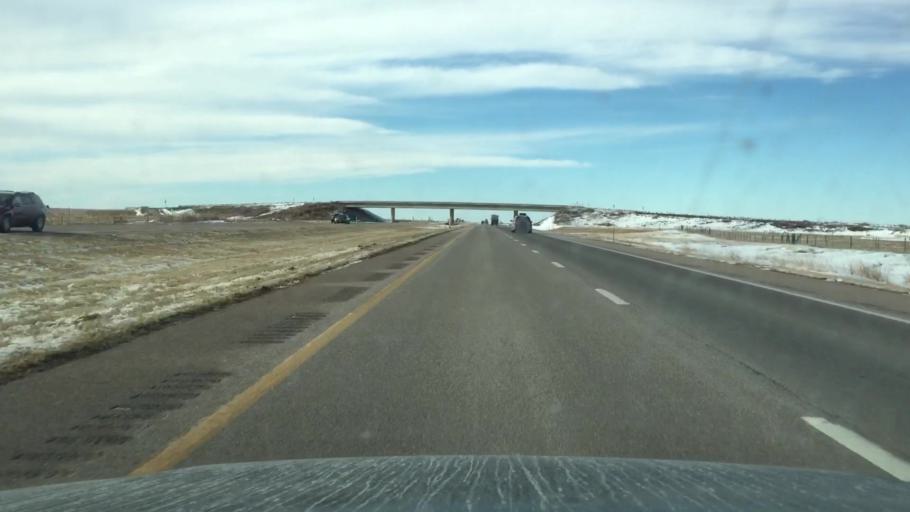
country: US
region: Kansas
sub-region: Gove County
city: Gove
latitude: 39.0745
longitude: -100.2765
